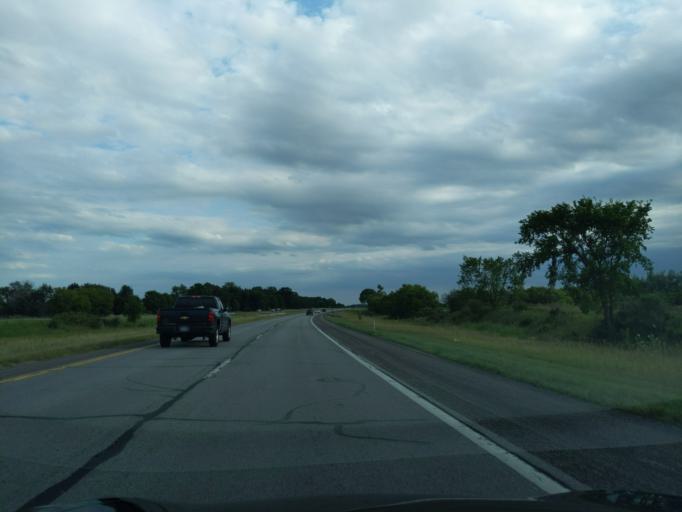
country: US
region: Michigan
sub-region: Clare County
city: Clare
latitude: 43.7454
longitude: -84.7587
